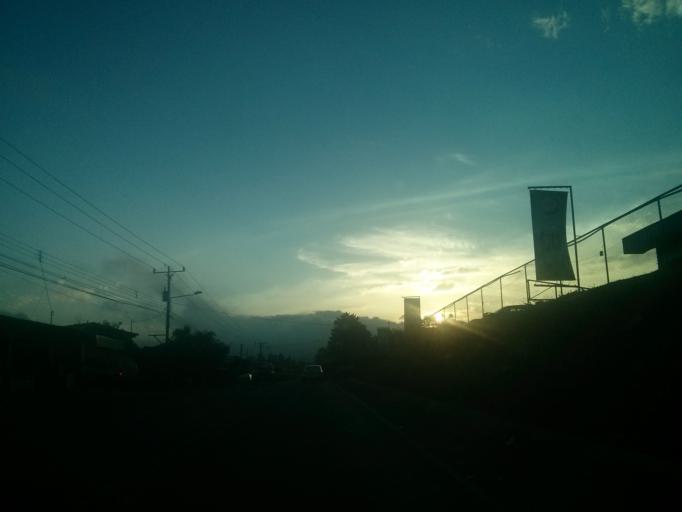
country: CR
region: Cartago
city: Cartago
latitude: 9.8783
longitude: -83.9073
